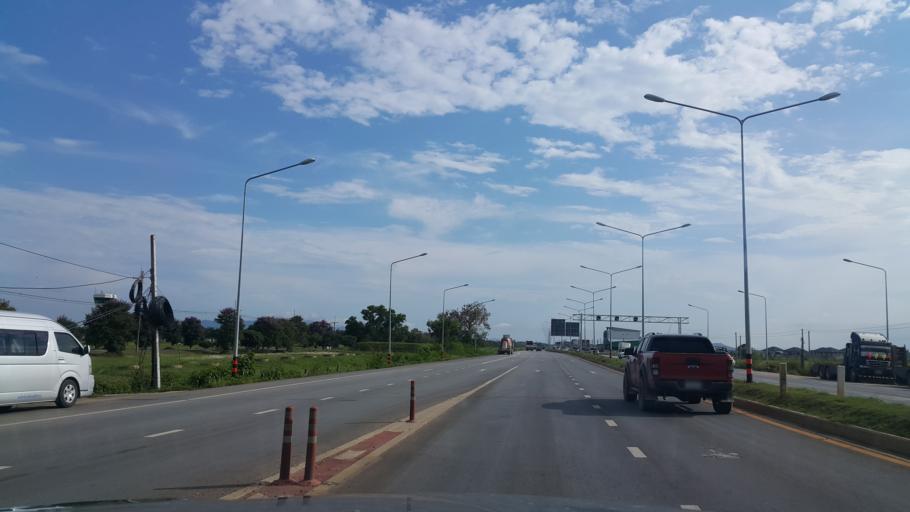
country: TH
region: Chiang Rai
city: Chiang Rai
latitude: 19.9533
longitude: 99.8761
